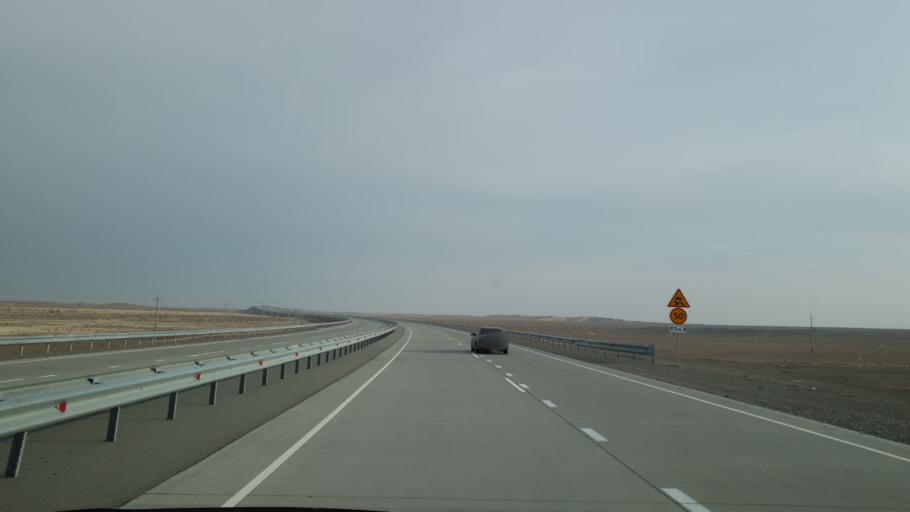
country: KZ
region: Almaty Oblysy
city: Kegen
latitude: 43.7590
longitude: 79.1367
